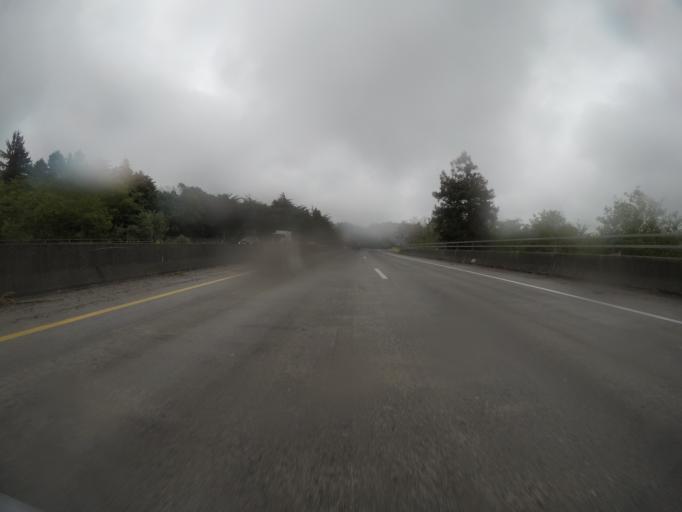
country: US
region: California
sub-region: Humboldt County
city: Arcata
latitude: 40.8917
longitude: -124.0806
